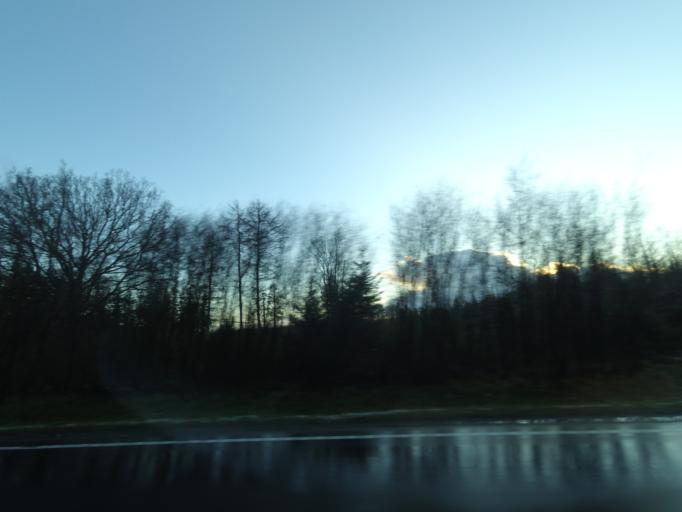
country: DK
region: Central Jutland
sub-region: Ikast-Brande Kommune
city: Brande
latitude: 56.0104
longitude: 9.0590
